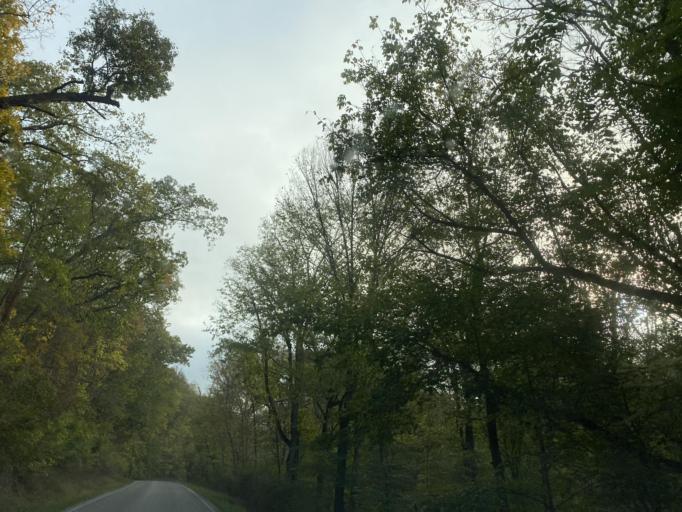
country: US
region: Kentucky
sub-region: Pendleton County
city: Falmouth
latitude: 38.7251
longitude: -84.3111
